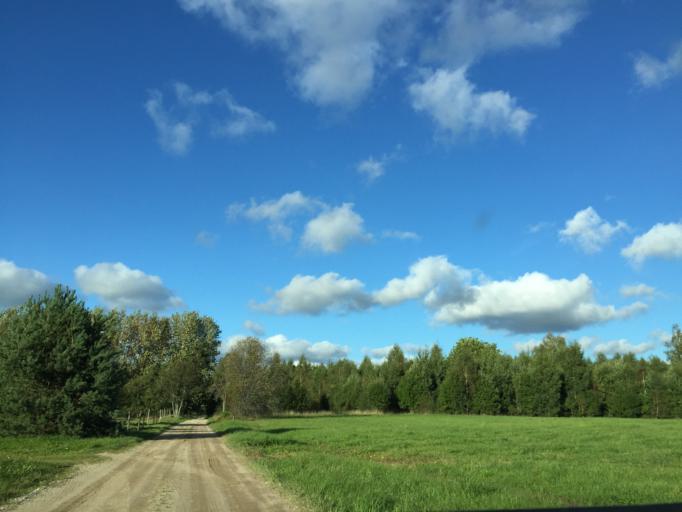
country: LV
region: Kuldigas Rajons
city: Kuldiga
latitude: 57.0084
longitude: 21.7614
